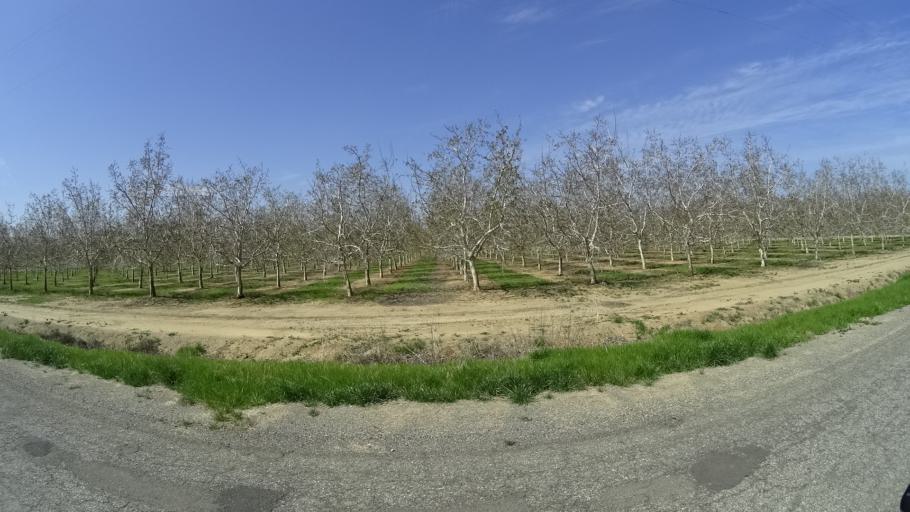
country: US
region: California
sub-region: Glenn County
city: Hamilton City
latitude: 39.6390
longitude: -122.0743
